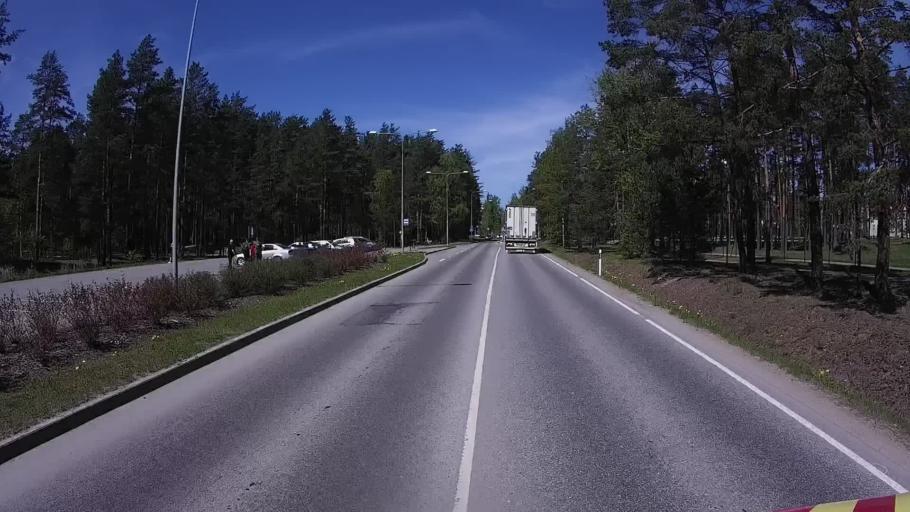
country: EE
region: Vorumaa
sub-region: Voru linn
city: Voru
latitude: 57.8233
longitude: 27.0180
